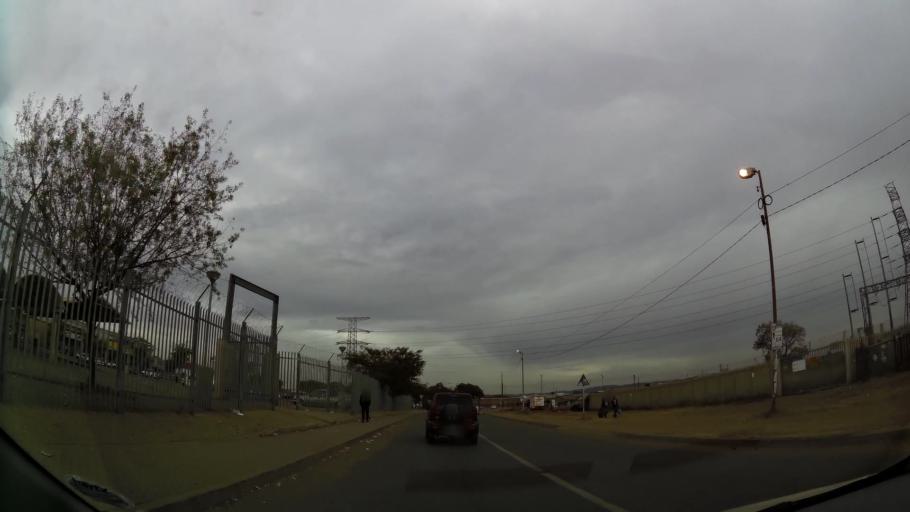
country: ZA
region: Gauteng
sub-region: City of Tshwane Metropolitan Municipality
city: Pretoria
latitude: -25.7146
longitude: 28.3308
